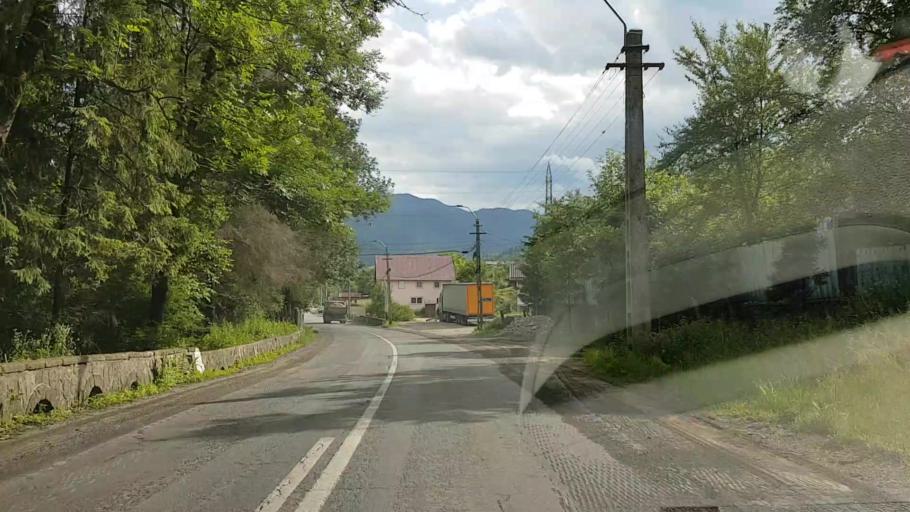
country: RO
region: Neamt
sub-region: Comuna Bicaz
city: Dodeni
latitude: 46.9298
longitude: 26.0956
